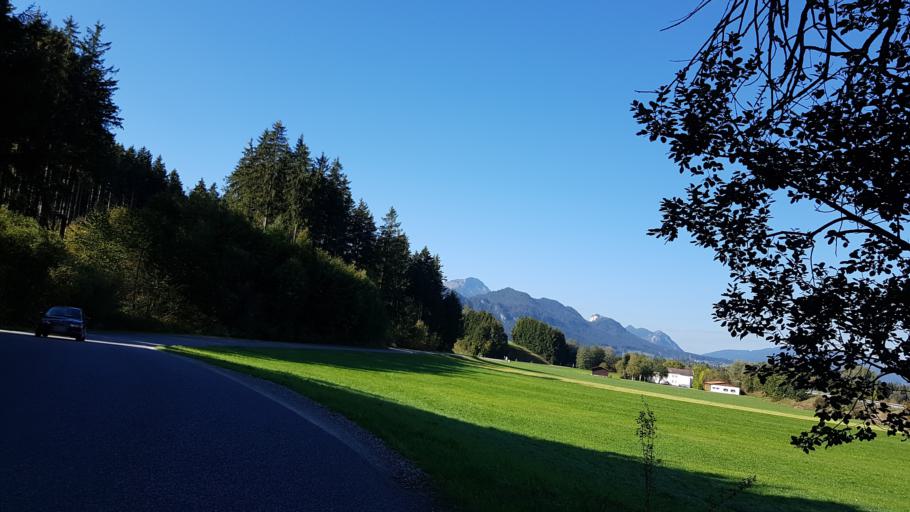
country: DE
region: Bavaria
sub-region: Swabia
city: Fuessen
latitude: 47.5797
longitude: 10.6851
